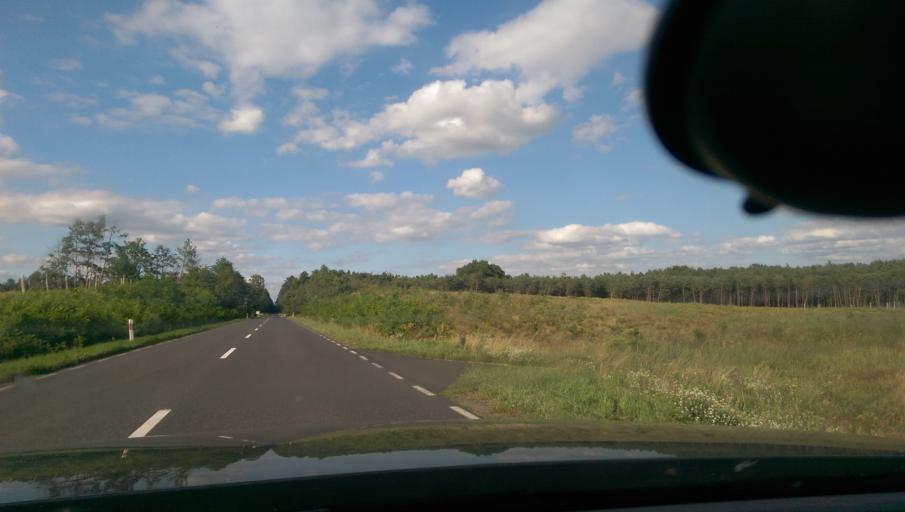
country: PL
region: Lubusz
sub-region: Powiat slubicki
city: Osno Lubuskie
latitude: 52.5278
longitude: 14.9293
